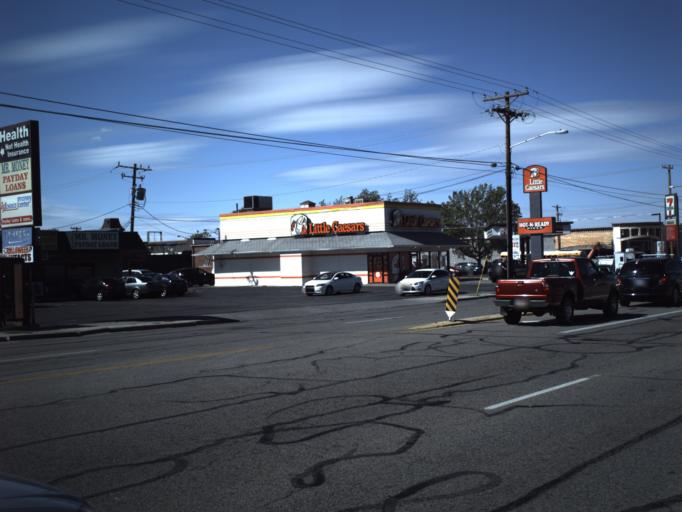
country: US
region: Utah
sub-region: Salt Lake County
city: Taylorsville
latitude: 40.6811
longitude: -111.9388
